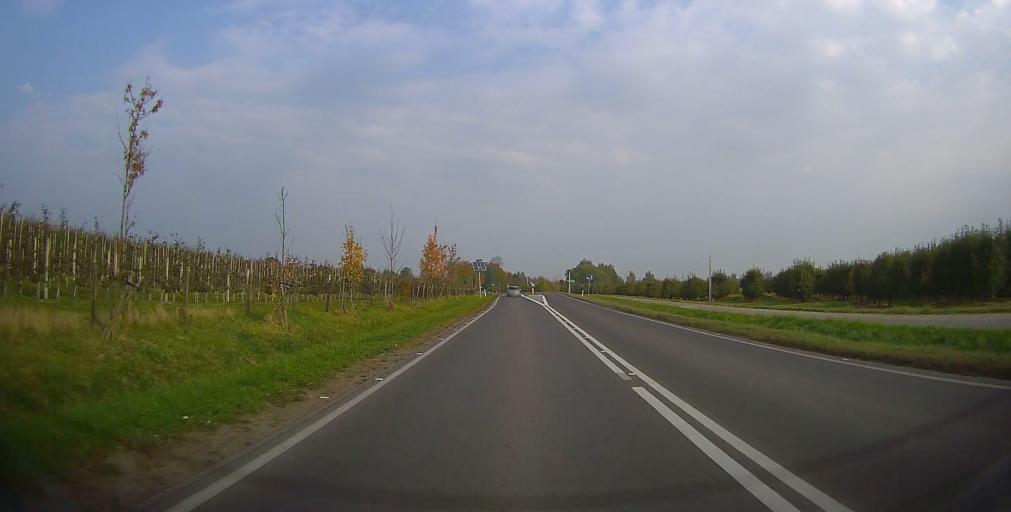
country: PL
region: Masovian Voivodeship
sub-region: Powiat grojecki
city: Mogielnica
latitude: 51.7431
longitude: 20.7615
